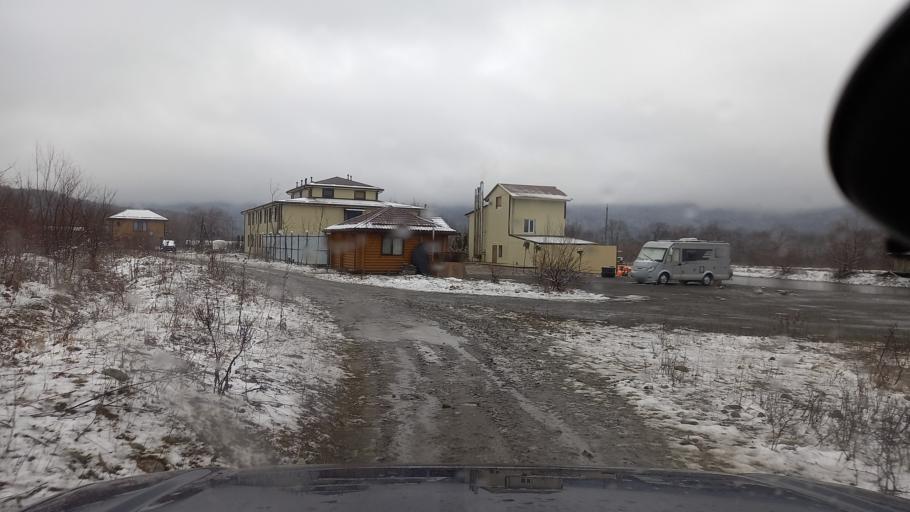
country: RU
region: Adygeya
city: Kamennomostskiy
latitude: 44.2286
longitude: 40.1821
